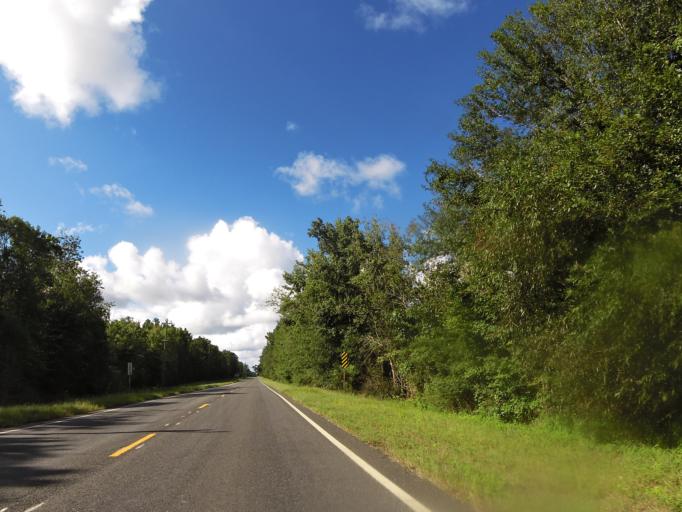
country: US
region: Georgia
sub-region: Camden County
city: Kingsland
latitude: 30.8629
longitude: -81.7028
